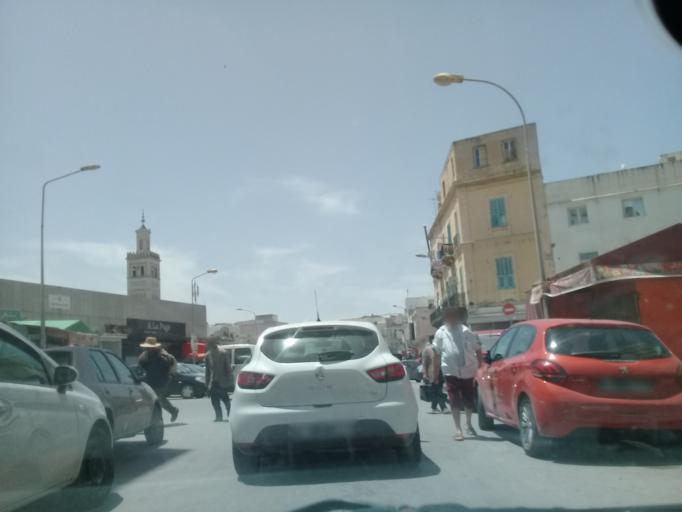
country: TN
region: Tunis
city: Tunis
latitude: 36.7932
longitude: 10.1773
